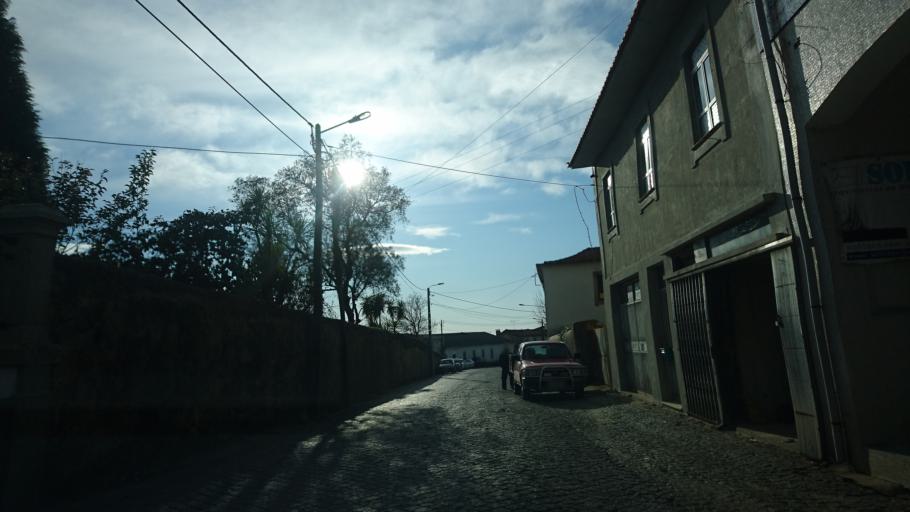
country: PT
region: Aveiro
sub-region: Santa Maria da Feira
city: Pacos de Brandao
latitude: 40.9715
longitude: -8.5860
